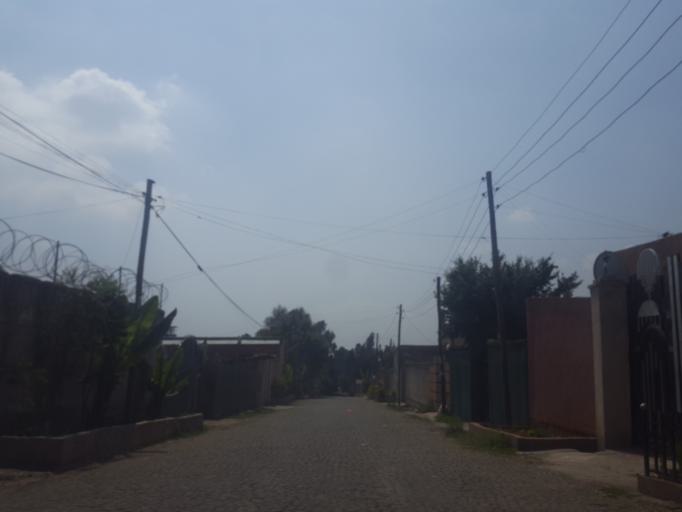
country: ET
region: Adis Abeba
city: Addis Ababa
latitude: 9.0641
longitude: 38.7235
